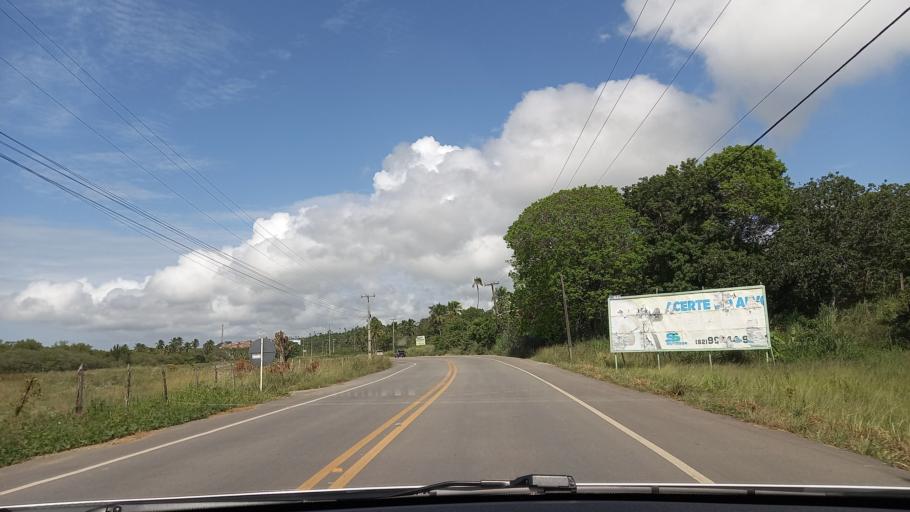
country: BR
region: Alagoas
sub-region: Maragogi
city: Maragogi
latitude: -8.9923
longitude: -35.2060
